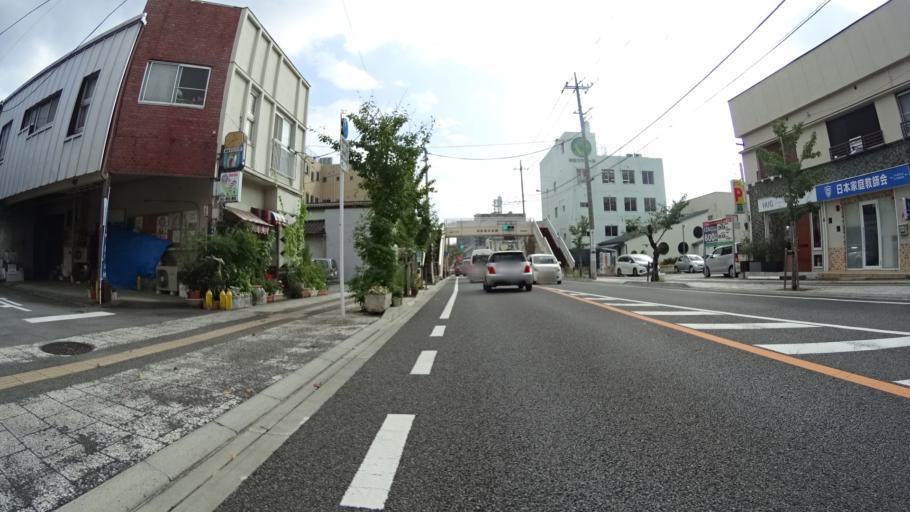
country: JP
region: Yamanashi
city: Kofu-shi
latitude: 35.6717
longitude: 138.5705
